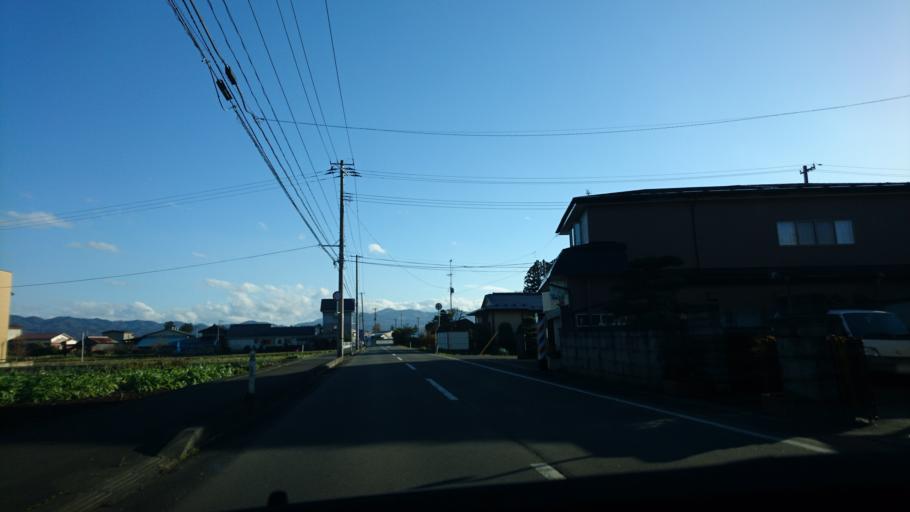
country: JP
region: Iwate
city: Mizusawa
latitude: 39.1106
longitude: 141.1557
